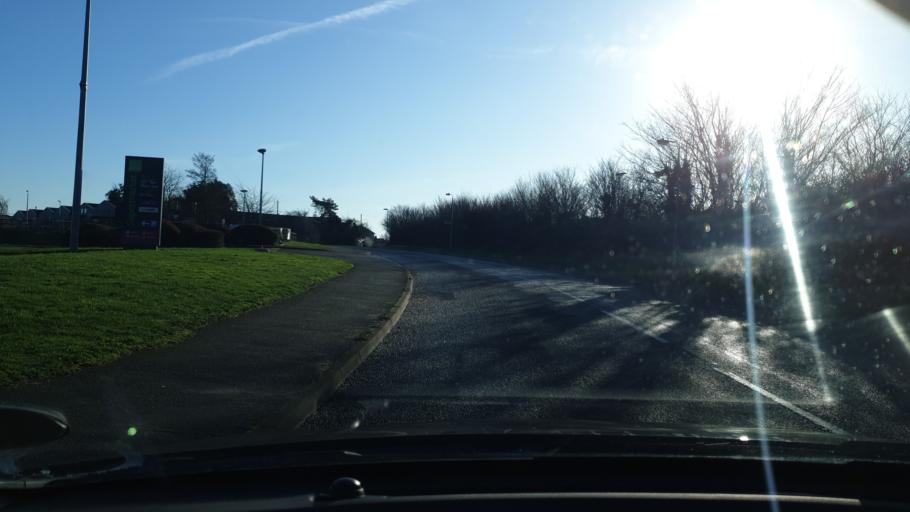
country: GB
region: England
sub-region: Essex
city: Brightlingsea
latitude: 51.8219
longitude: 1.0233
